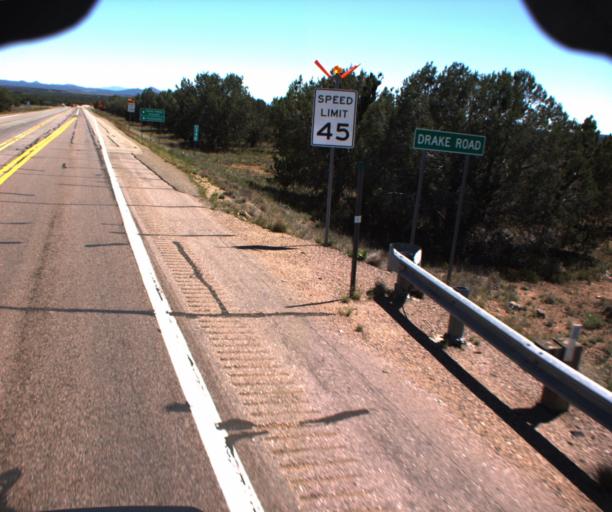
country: US
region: Arizona
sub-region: Yavapai County
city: Paulden
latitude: 35.0073
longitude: -112.3903
